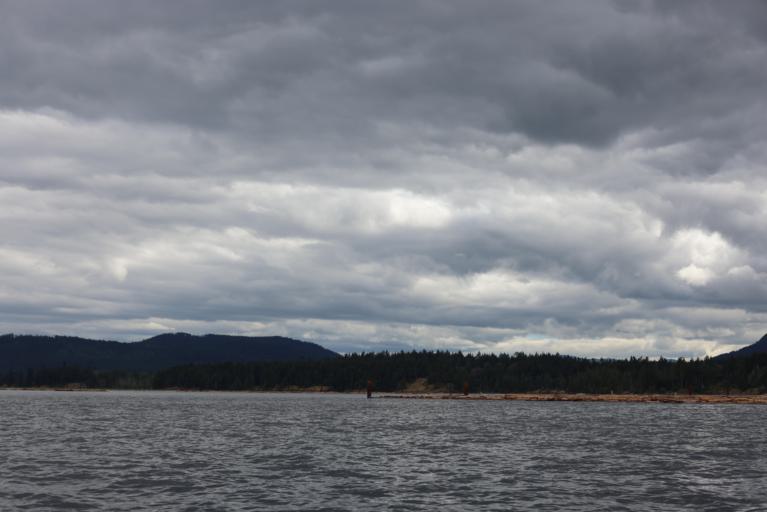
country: CA
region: British Columbia
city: North Cowichan
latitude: 48.9177
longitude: -123.6878
